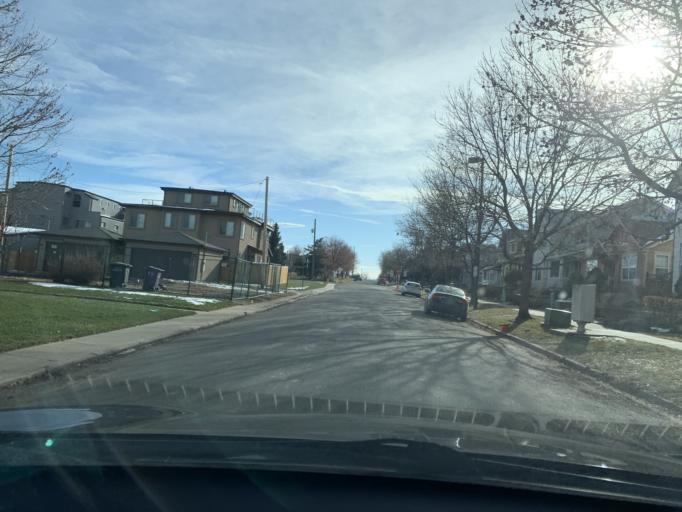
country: US
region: Colorado
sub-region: Jefferson County
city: Edgewater
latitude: 39.7484
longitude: -105.0316
